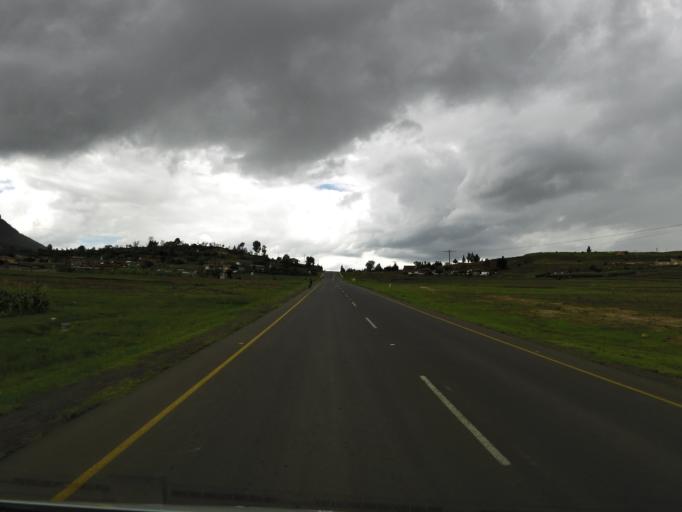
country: LS
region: Maseru
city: Maseru
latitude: -29.4967
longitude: 27.5282
